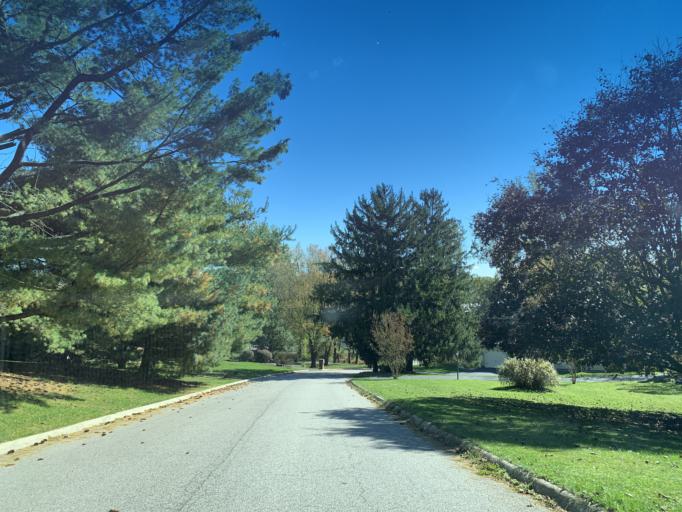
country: US
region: Maryland
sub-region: Harford County
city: Bel Air South
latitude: 39.5200
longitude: -76.3180
